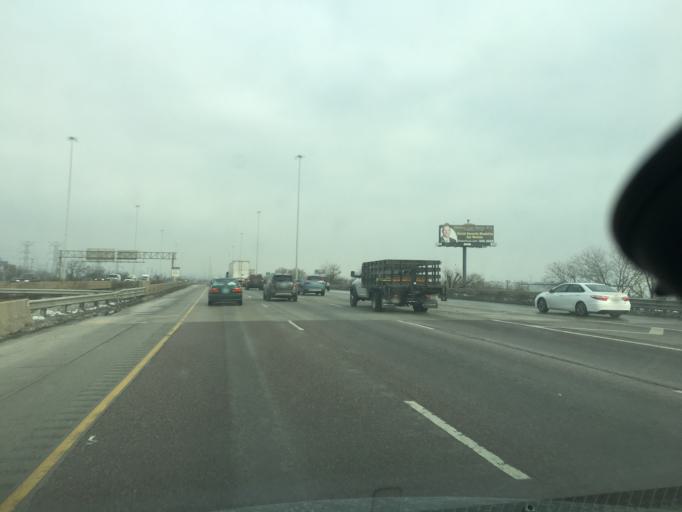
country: US
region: Illinois
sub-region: Cook County
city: Cicero
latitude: 41.8182
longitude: -87.7396
